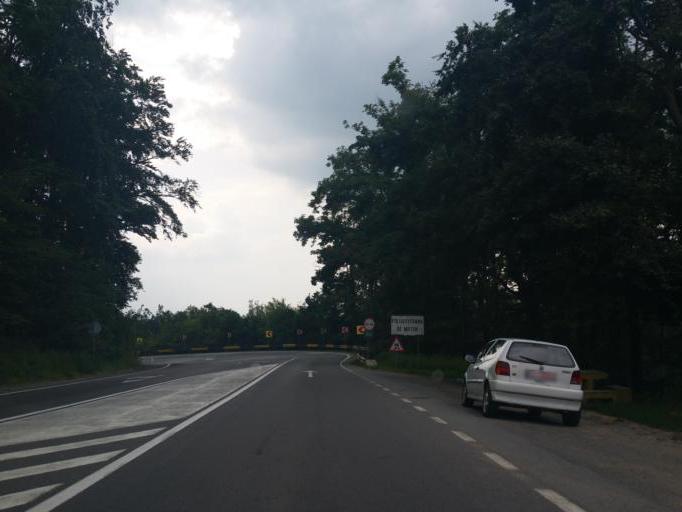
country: RO
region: Salaj
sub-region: Comuna Treznea
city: Treznea
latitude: 47.1456
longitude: 23.0881
